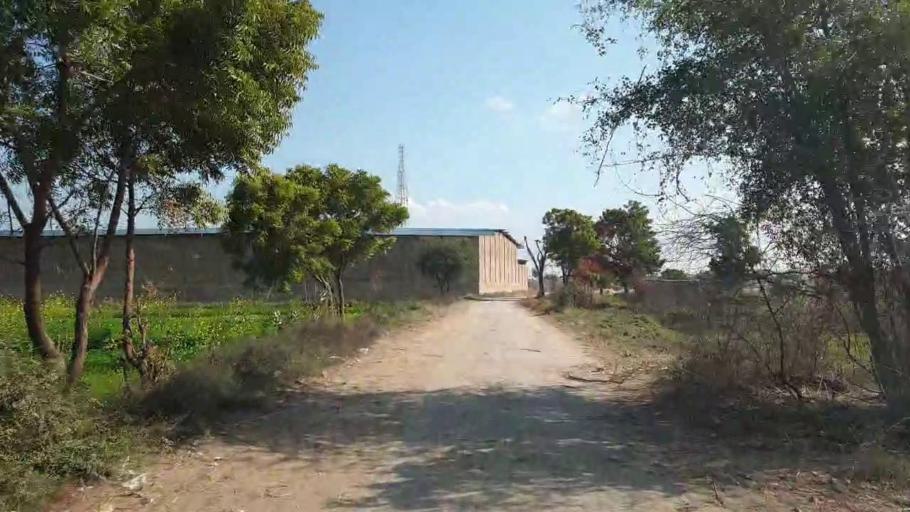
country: PK
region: Sindh
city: Shahpur Chakar
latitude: 26.0612
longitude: 68.5805
